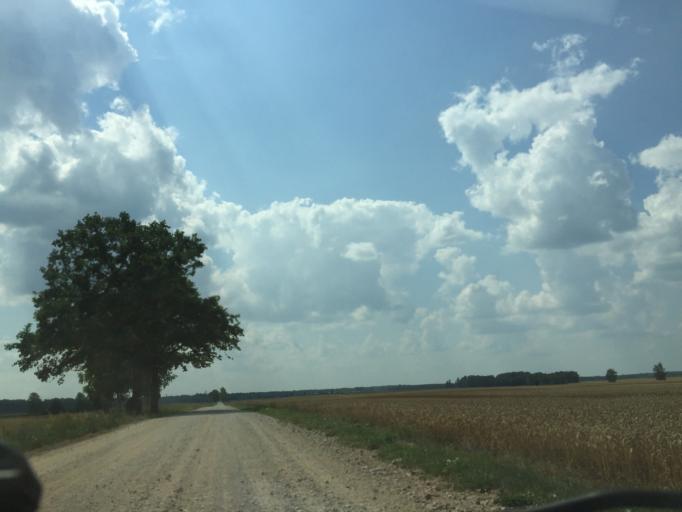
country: LT
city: Zagare
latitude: 56.3911
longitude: 23.1950
